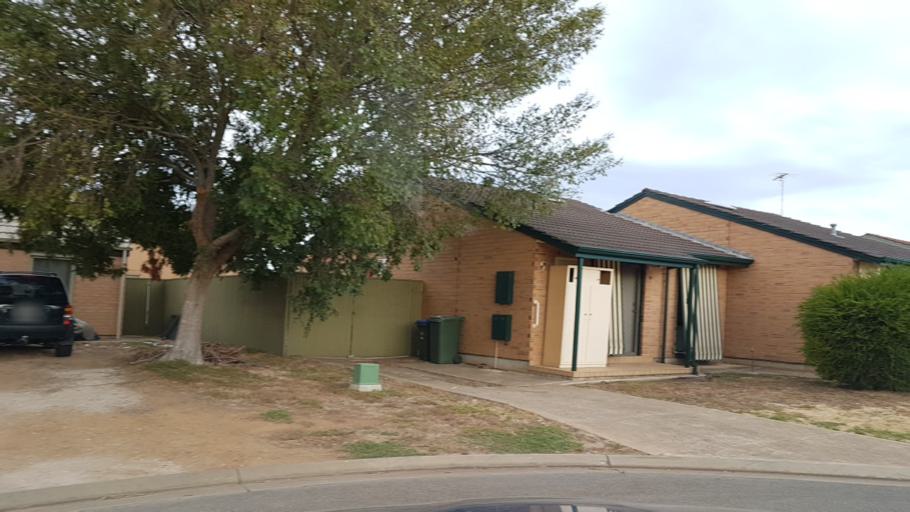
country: AU
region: South Australia
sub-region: Port Adelaide Enfield
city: Alberton
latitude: -34.8574
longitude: 138.5340
